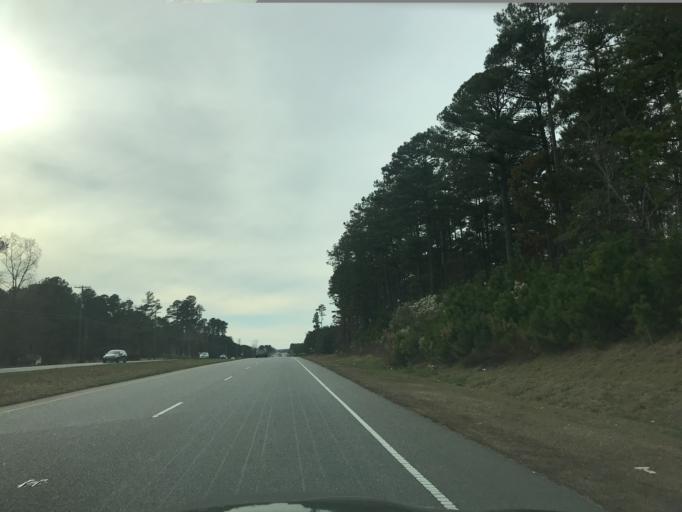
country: US
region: North Carolina
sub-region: Wake County
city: Rolesville
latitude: 35.9008
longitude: -78.4946
